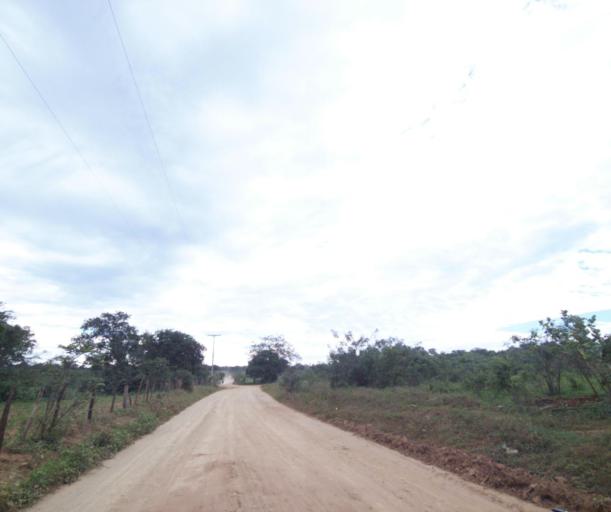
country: BR
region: Bahia
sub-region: Carinhanha
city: Carinhanha
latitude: -14.1804
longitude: -44.5228
